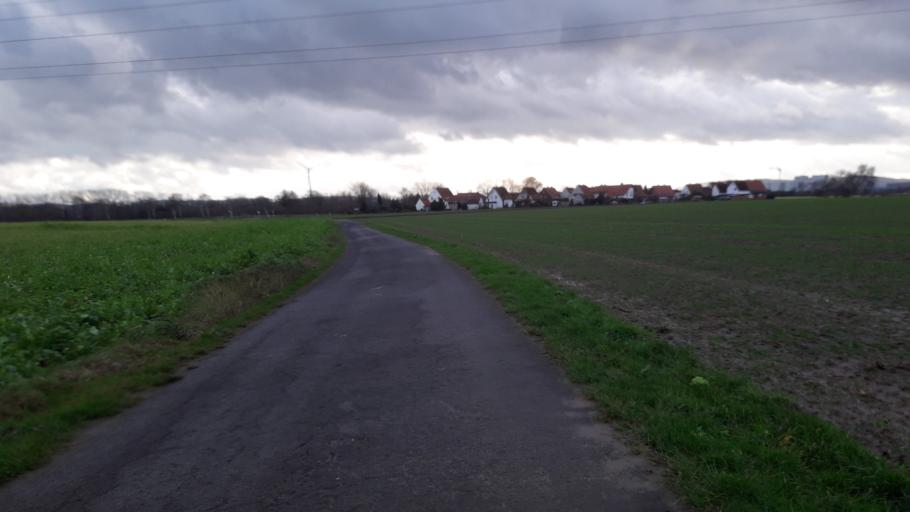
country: DE
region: North Rhine-Westphalia
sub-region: Regierungsbezirk Detmold
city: Petershagen
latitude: 52.3192
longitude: 8.9711
